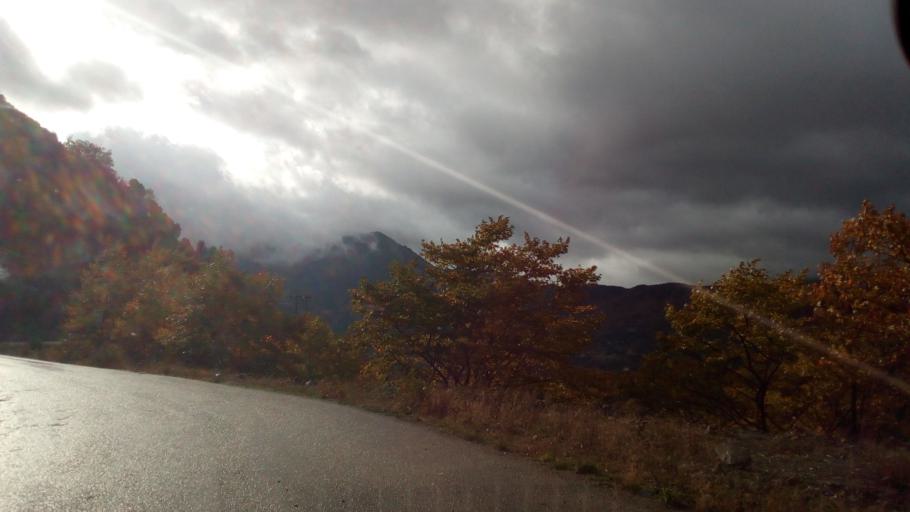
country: GR
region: West Greece
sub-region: Nomos Aitolias kai Akarnanias
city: Thermo
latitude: 38.6824
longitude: 21.8486
